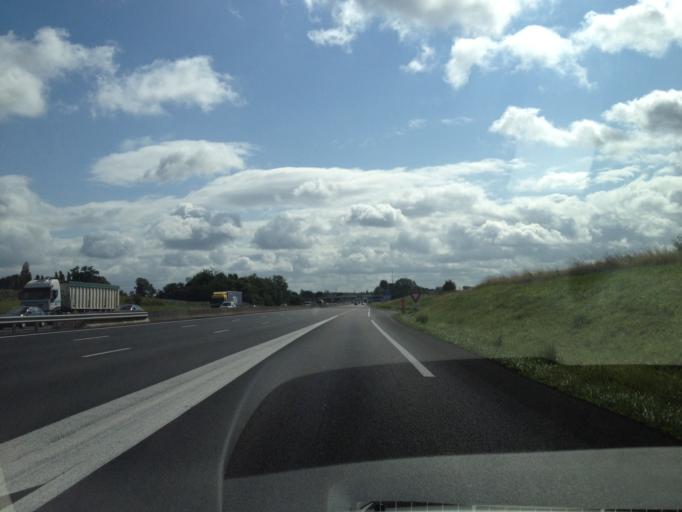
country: FR
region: Haute-Normandie
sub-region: Departement de l'Eure
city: Bourg-Achard
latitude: 49.3635
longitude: 0.8373
